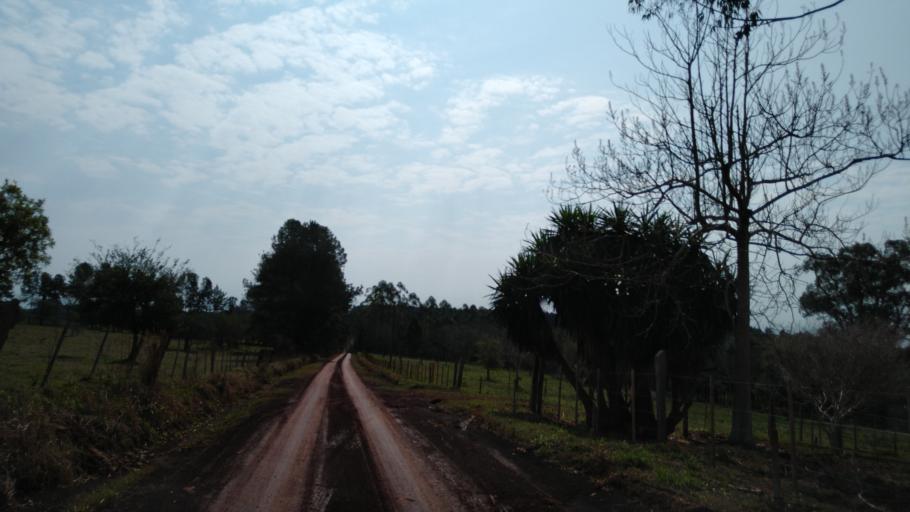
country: AR
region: Misiones
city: Capiovi
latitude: -26.9506
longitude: -55.0443
